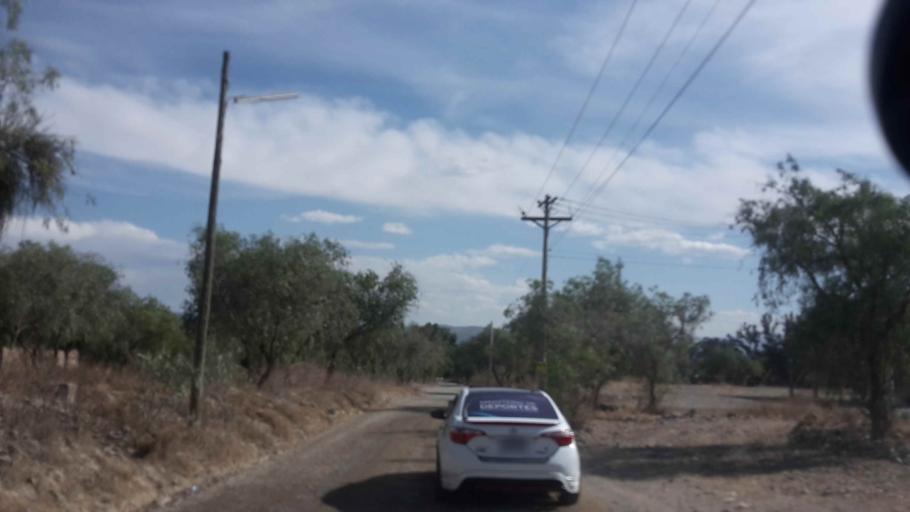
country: BO
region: Cochabamba
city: Cochabamba
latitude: -17.3383
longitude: -66.2117
